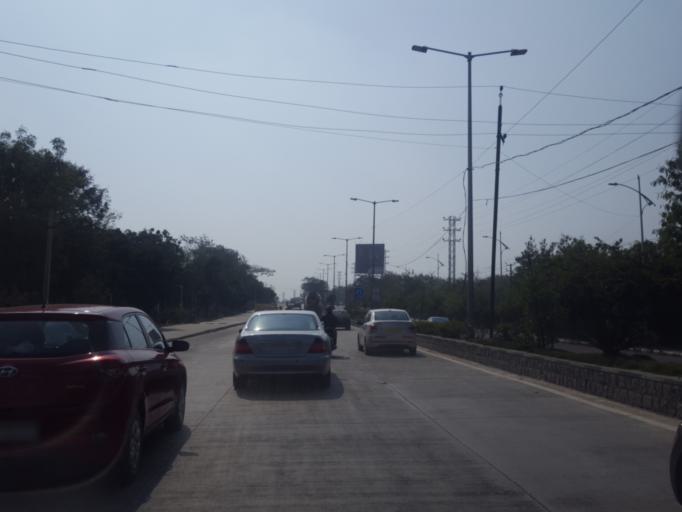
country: IN
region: Telangana
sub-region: Medak
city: Serilingampalle
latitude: 17.4438
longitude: 78.3510
